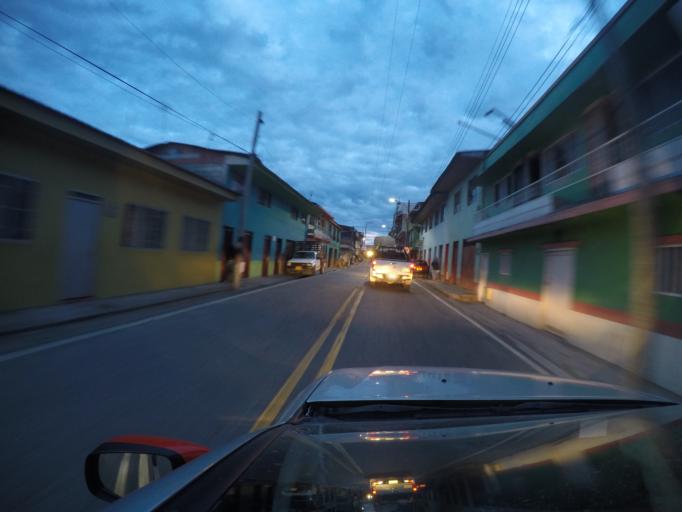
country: CO
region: Tolima
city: Herveo
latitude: 5.1336
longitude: -75.1443
